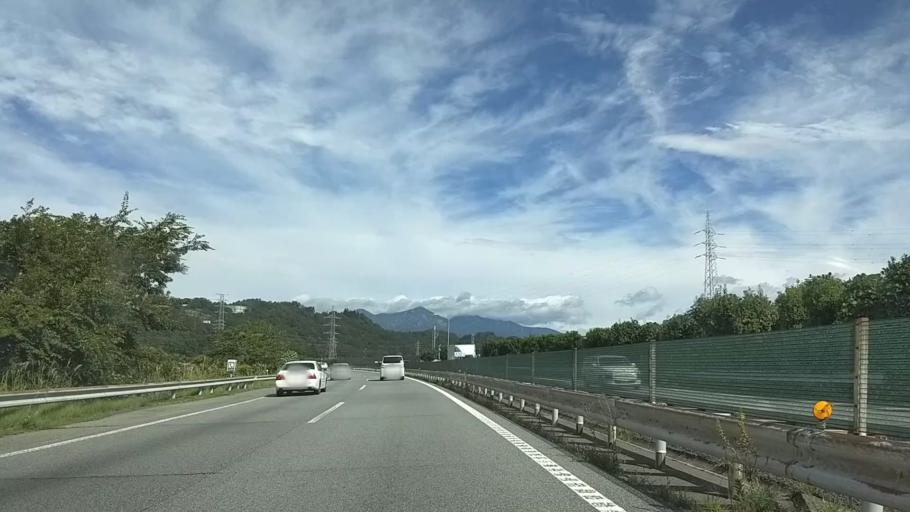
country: JP
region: Yamanashi
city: Nirasaki
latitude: 35.7801
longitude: 138.4221
